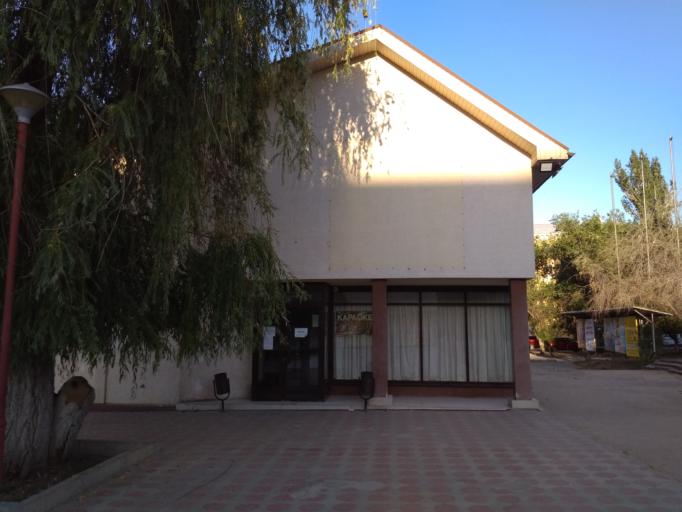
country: RU
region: Volgograd
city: Vodstroy
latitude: 48.8042
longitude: 44.5959
